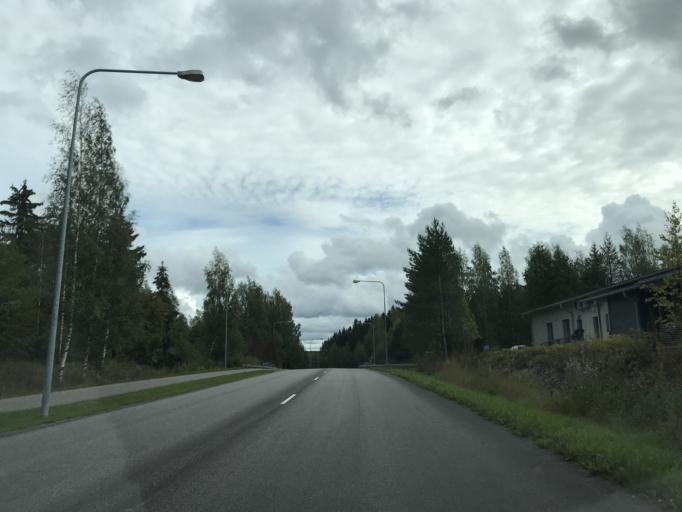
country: FI
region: Paijanne Tavastia
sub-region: Lahti
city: Lahti
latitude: 61.0019
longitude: 25.7645
